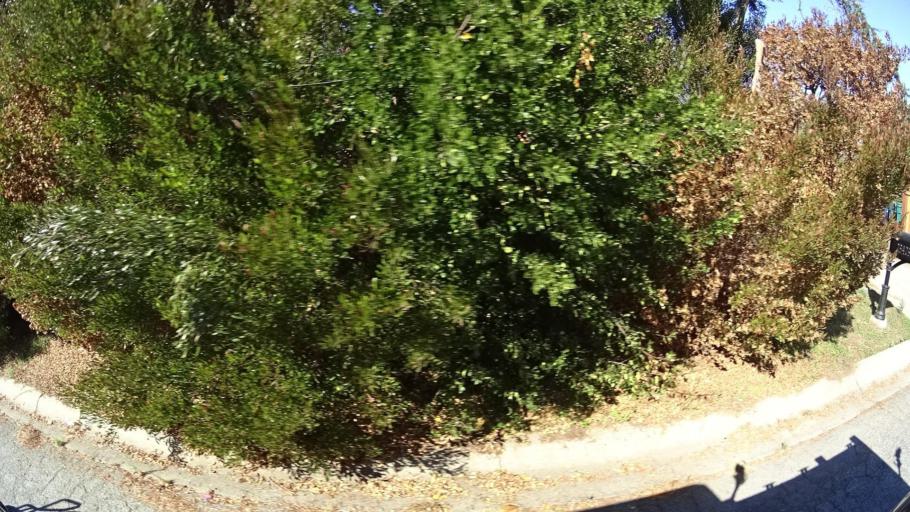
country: US
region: California
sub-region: Monterey County
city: Carmel-by-the-Sea
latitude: 36.5400
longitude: -121.8804
